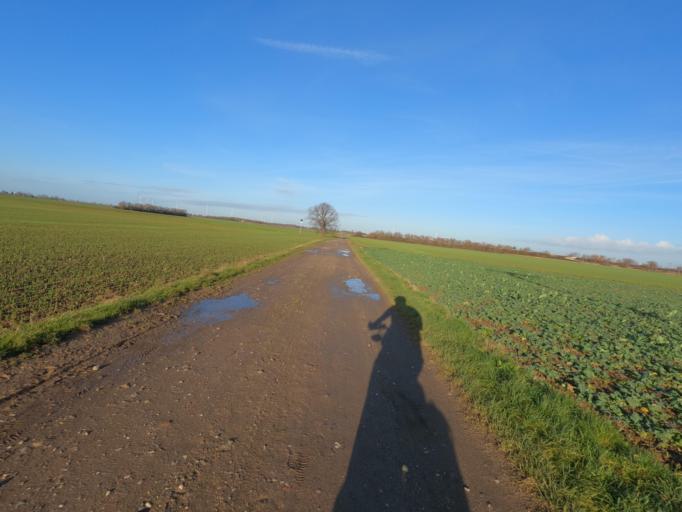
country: DE
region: North Rhine-Westphalia
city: Julich
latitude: 50.9422
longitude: 6.3942
